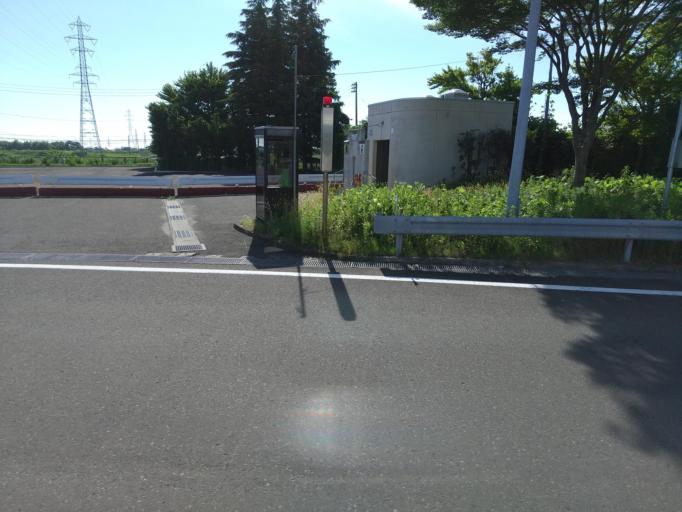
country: JP
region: Miyagi
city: Sendai
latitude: 38.2149
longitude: 140.9047
